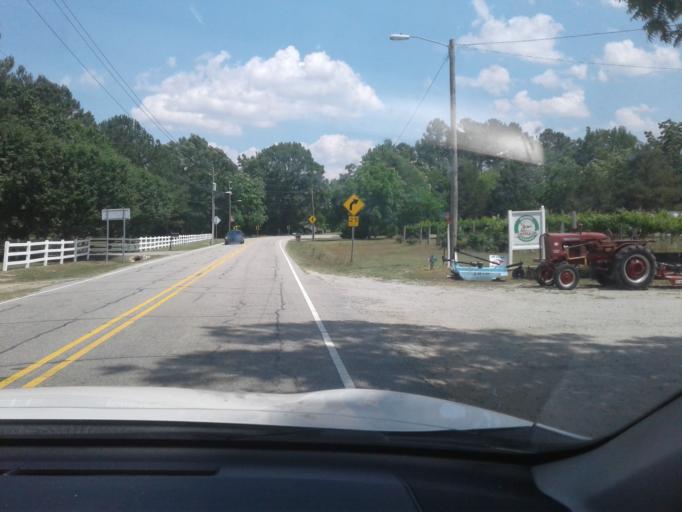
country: US
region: North Carolina
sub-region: Harnett County
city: Erwin
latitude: 35.2160
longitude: -78.6773
